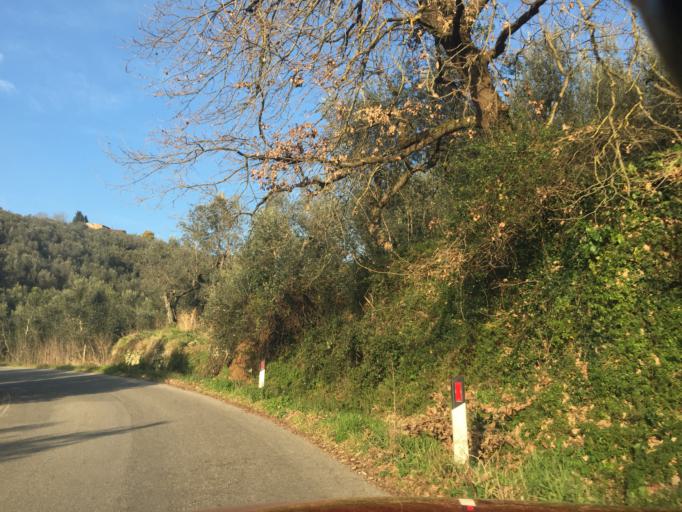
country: IT
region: Tuscany
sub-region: Province of Florence
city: Vinci
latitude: 43.8010
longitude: 10.9309
